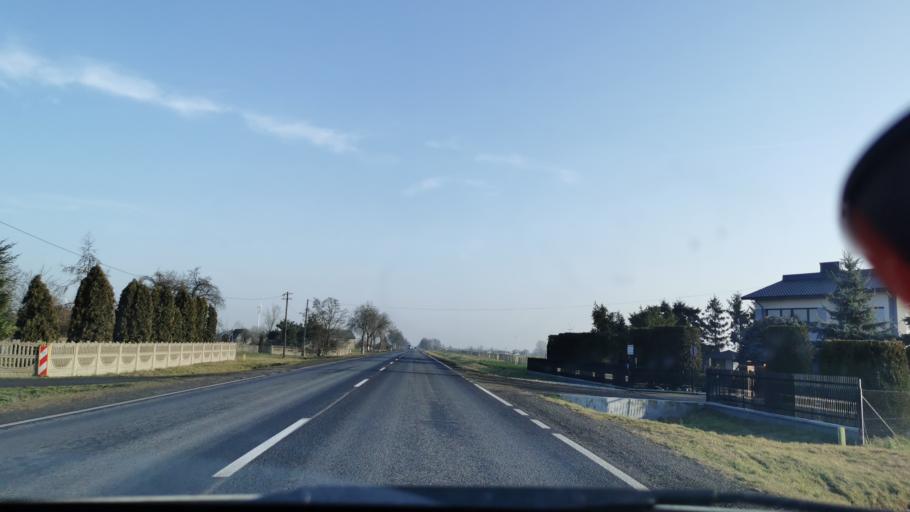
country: PL
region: Lodz Voivodeship
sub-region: Powiat sieradzki
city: Blaszki
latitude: 51.6723
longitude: 18.3679
